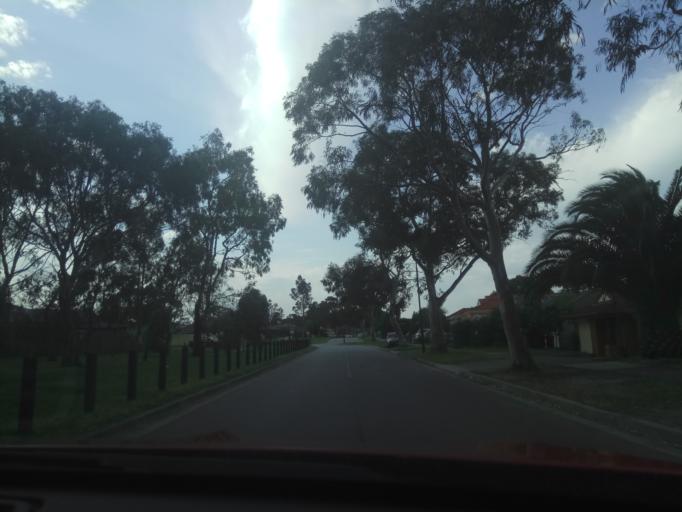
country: AU
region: Victoria
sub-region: Casey
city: Lynbrook
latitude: -38.0483
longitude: 145.2508
